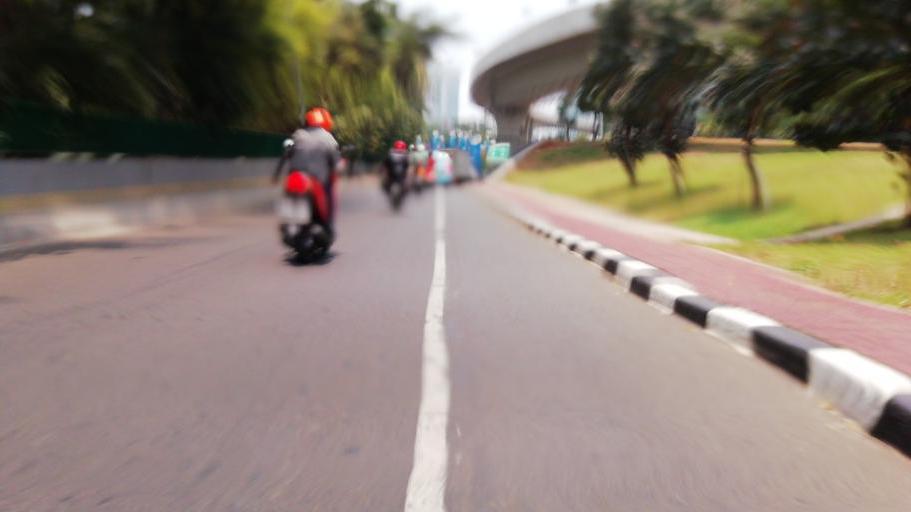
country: ID
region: Jakarta Raya
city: Jakarta
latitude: -6.2197
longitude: 106.8107
